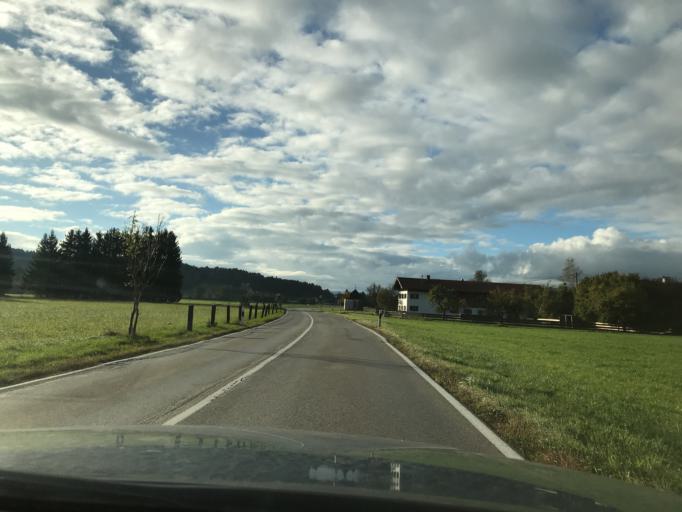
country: DE
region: Bavaria
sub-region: Upper Bavaria
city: Konigsdorf
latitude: 47.8366
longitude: 11.5300
